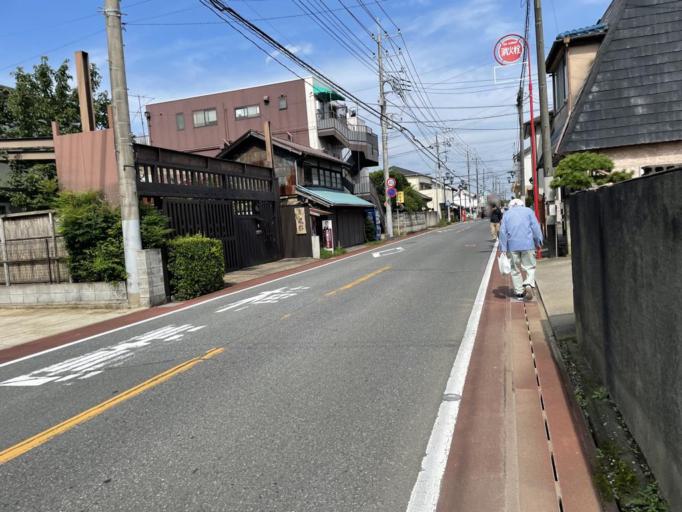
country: JP
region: Chiba
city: Sakura
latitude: 35.7182
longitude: 140.2348
